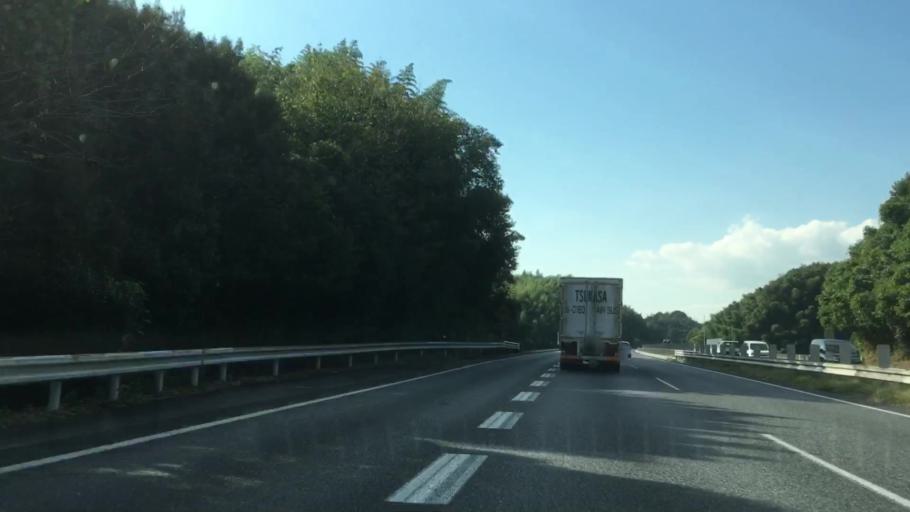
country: JP
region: Yamaguchi
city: Kudamatsu
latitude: 34.0310
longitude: 131.9371
